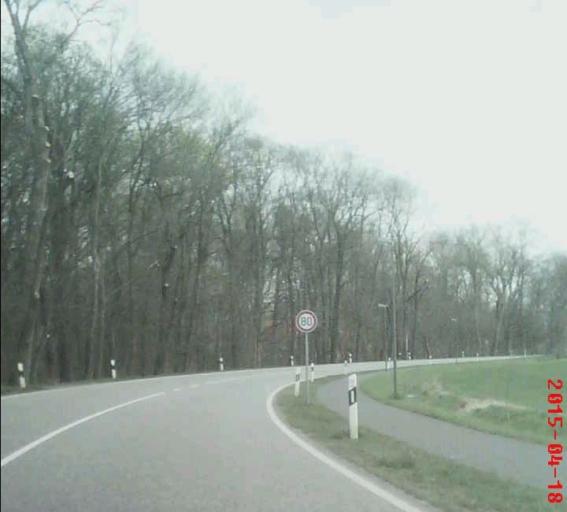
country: DE
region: Thuringia
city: Worbis
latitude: 51.4124
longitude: 10.3769
